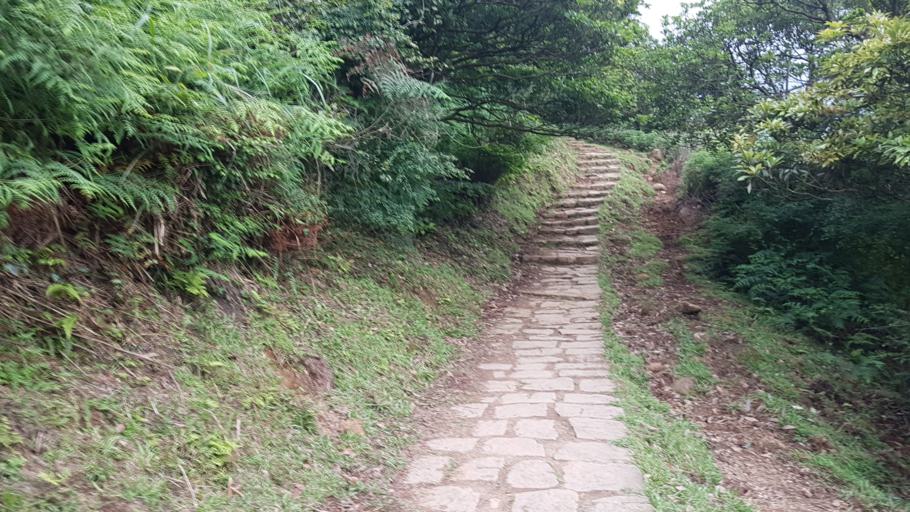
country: TW
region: Taipei
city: Taipei
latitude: 25.1625
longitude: 121.5780
